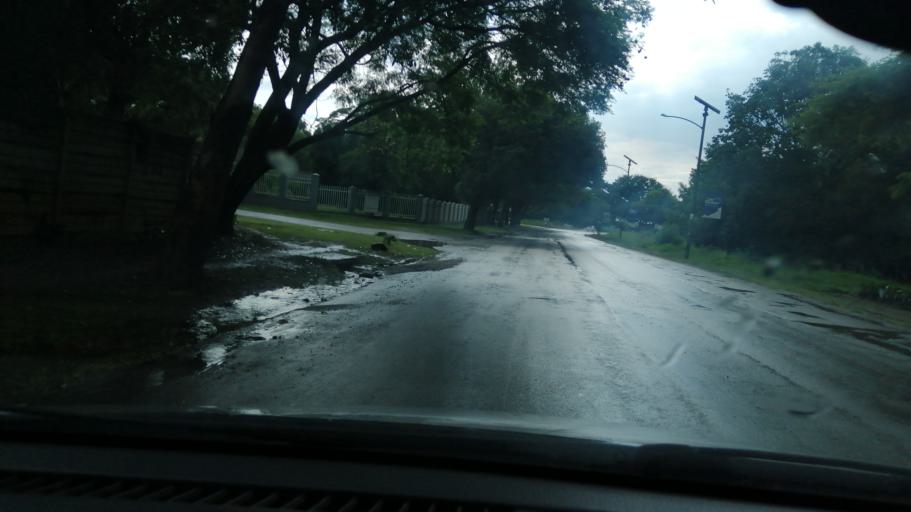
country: ZW
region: Harare
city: Harare
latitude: -17.7903
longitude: 31.0604
